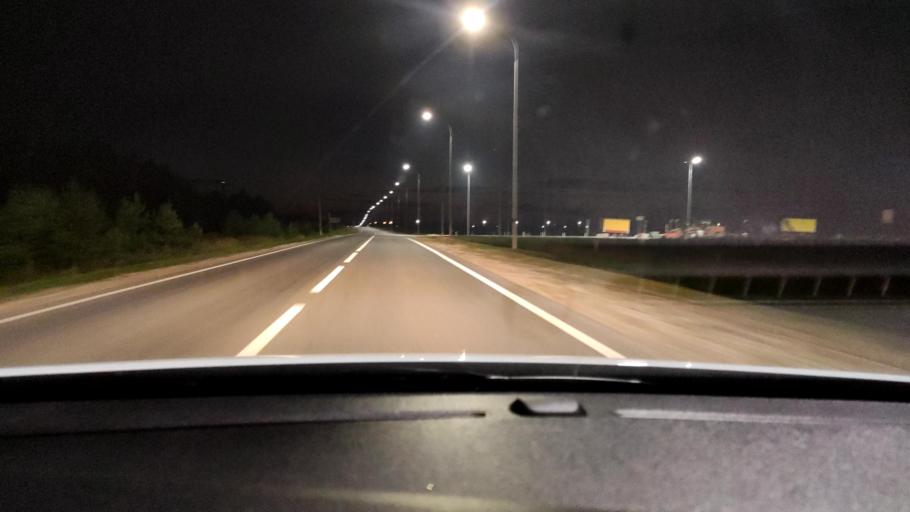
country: RU
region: Tatarstan
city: Sviyazhsk
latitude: 55.7369
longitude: 48.7373
